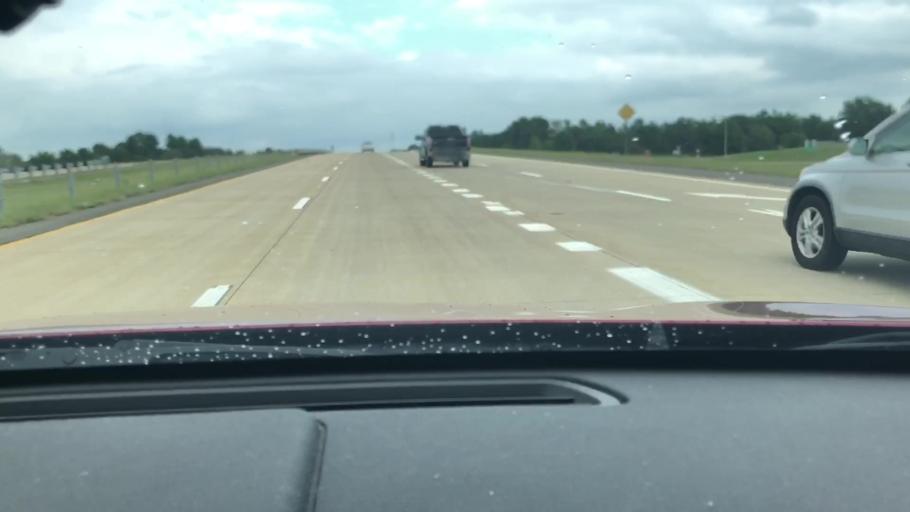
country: US
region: Texas
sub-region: Bowie County
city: Texarkana
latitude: 33.3918
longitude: -94.0148
